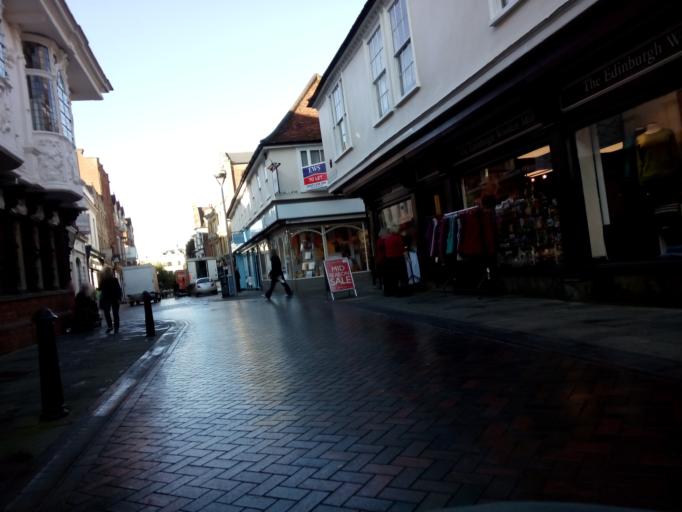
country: GB
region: England
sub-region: Suffolk
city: Ipswich
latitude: 52.0568
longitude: 1.1550
